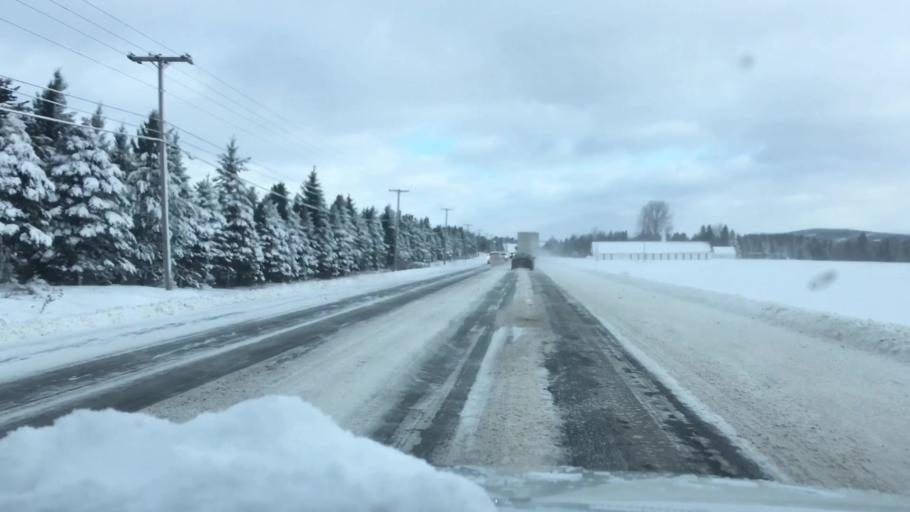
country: US
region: Maine
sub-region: Aroostook County
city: Presque Isle
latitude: 46.7337
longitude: -68.0005
